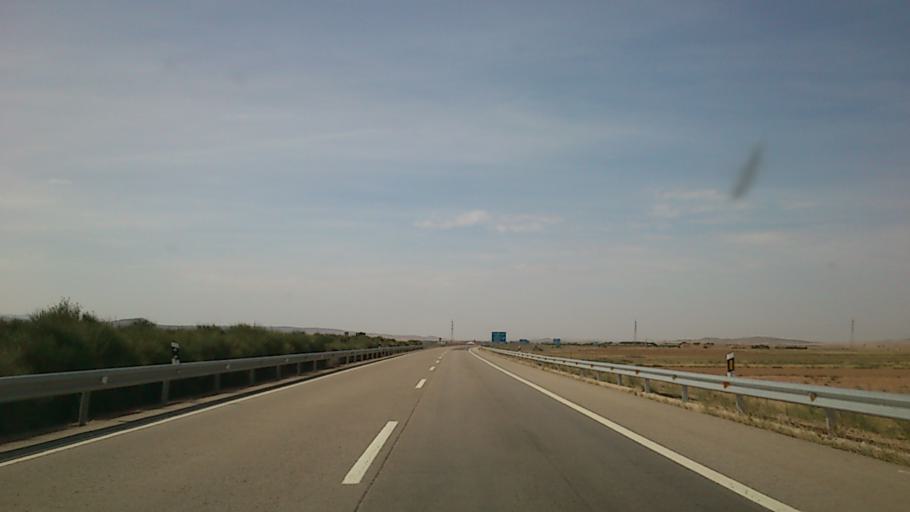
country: ES
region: Aragon
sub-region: Provincia de Teruel
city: Villarquemado
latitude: 40.5524
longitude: -1.2738
